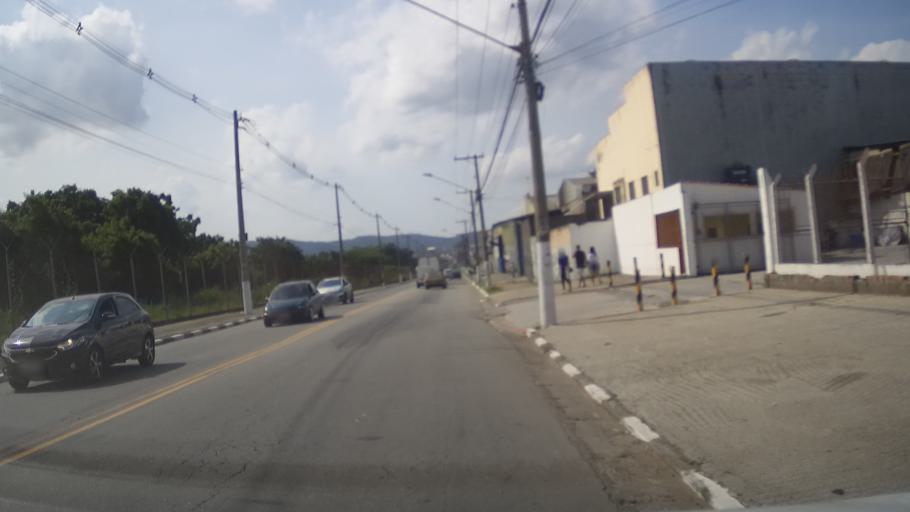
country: BR
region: Sao Paulo
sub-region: Guarulhos
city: Guarulhos
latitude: -23.4280
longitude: -46.4374
